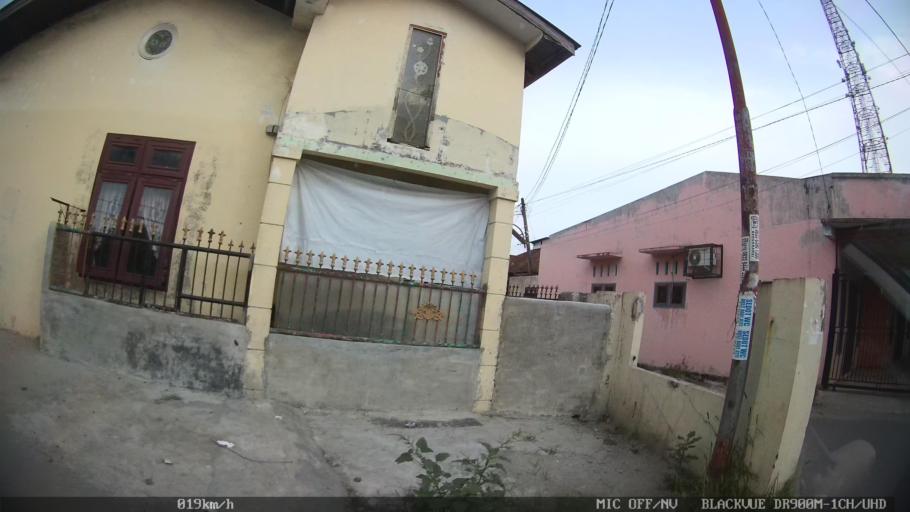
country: ID
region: North Sumatra
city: Medan
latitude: 3.5955
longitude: 98.7445
